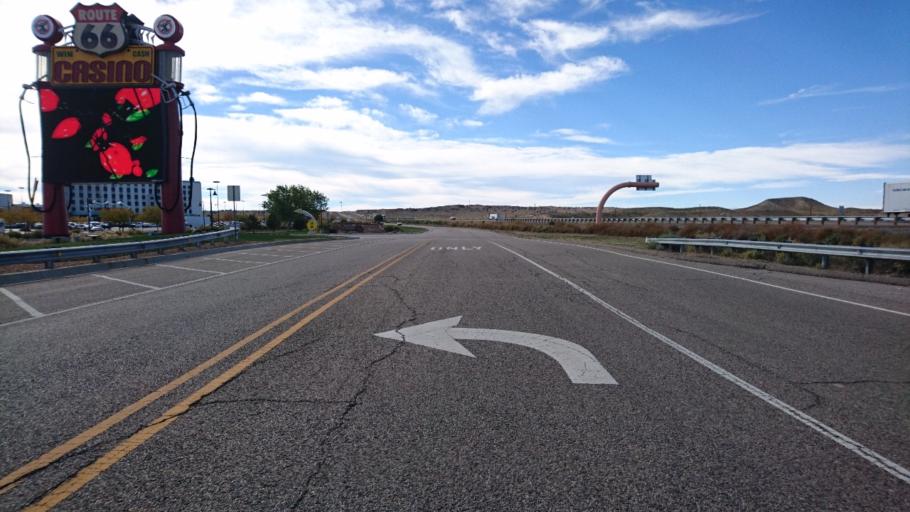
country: US
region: New Mexico
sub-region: Bernalillo County
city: South Valley
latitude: 35.0305
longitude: -106.9500
